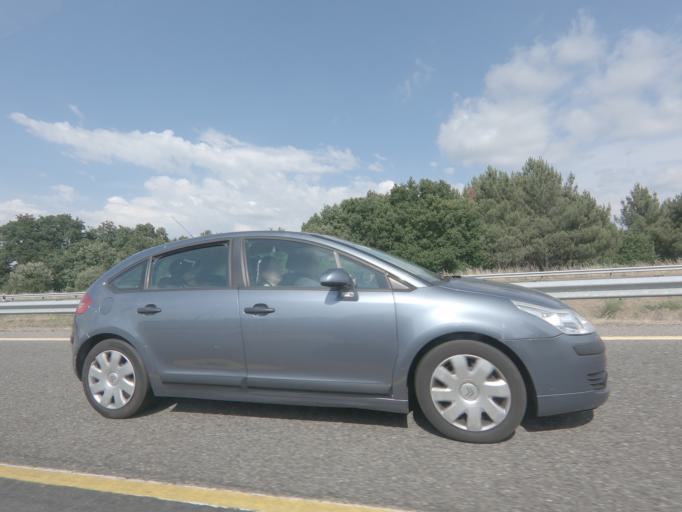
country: ES
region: Galicia
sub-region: Provincia de Ourense
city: Taboadela
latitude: 42.2613
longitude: -7.8685
